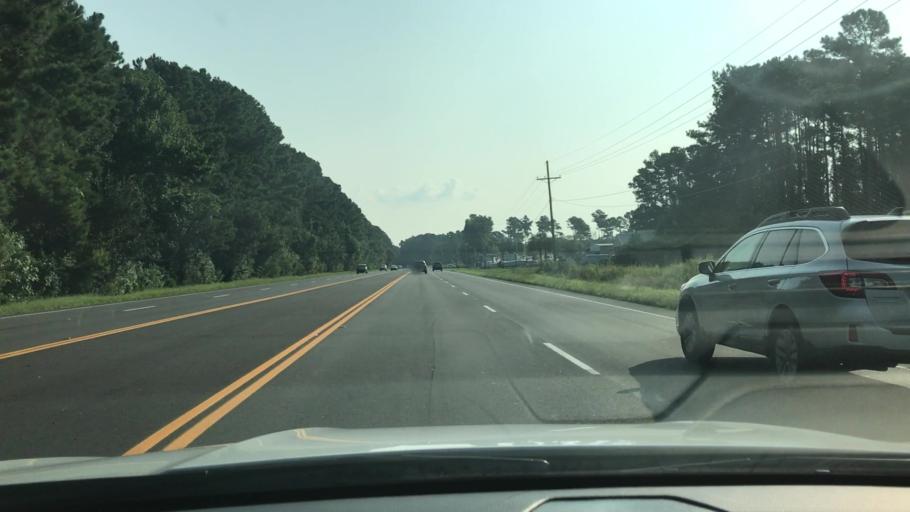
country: US
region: South Carolina
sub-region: Charleston County
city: Awendaw
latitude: 33.0967
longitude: -79.4740
